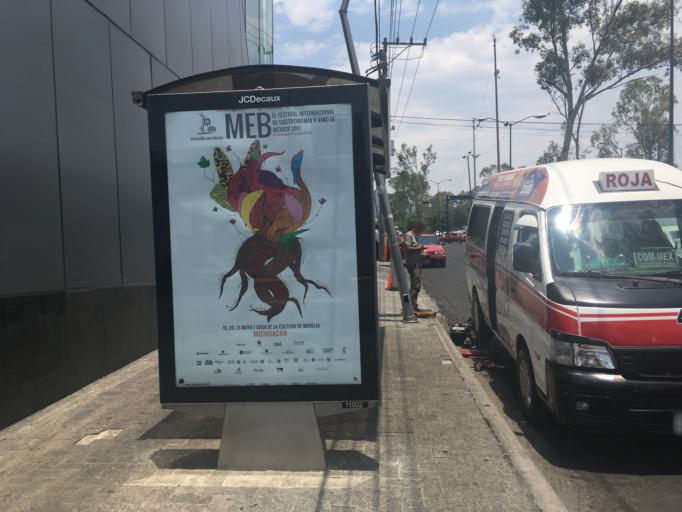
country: MX
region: Michoacan
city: Morelia
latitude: 19.6961
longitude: -101.1593
